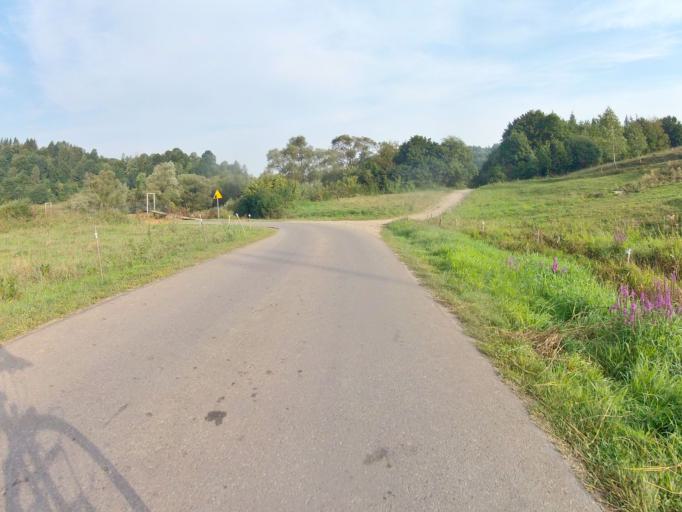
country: PL
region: Subcarpathian Voivodeship
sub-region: Powiat jasielski
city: Nowy Zmigrod
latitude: 49.5535
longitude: 21.5395
